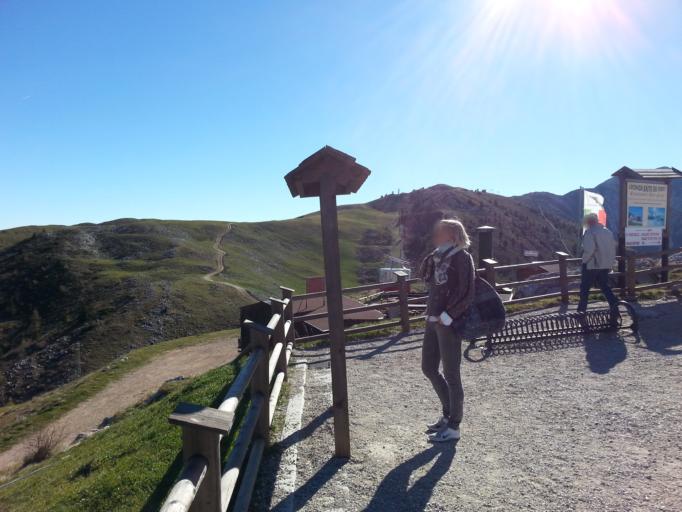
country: IT
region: Veneto
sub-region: Provincia di Verona
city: Malcesine
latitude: 45.7693
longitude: 10.8648
